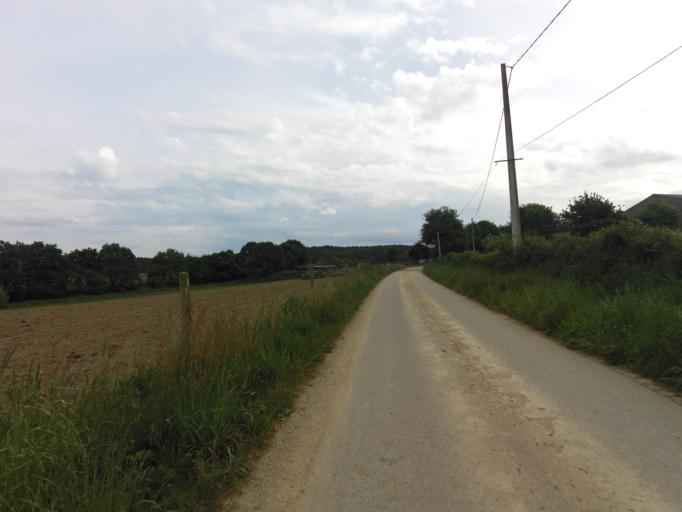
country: FR
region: Brittany
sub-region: Departement du Morbihan
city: Molac
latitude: 47.7630
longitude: -2.4232
